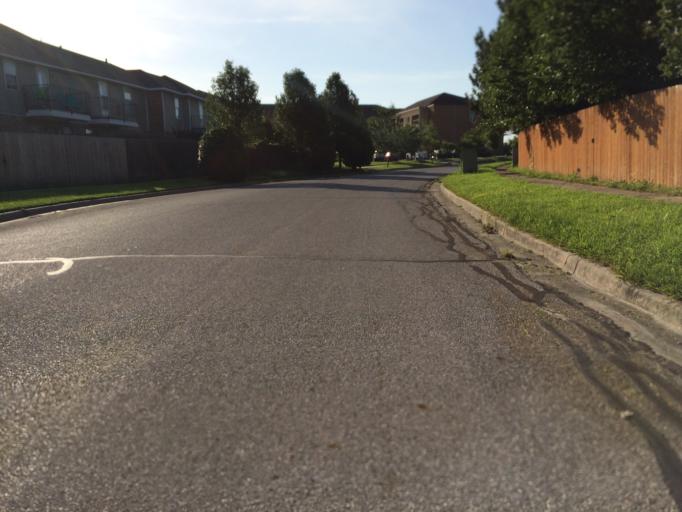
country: US
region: Oklahoma
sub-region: Cleveland County
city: Norman
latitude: 35.2283
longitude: -97.4892
